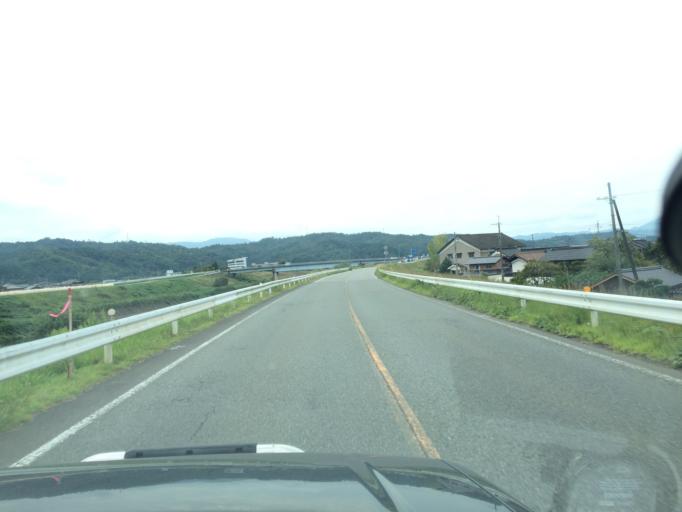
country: JP
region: Hyogo
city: Toyooka
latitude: 35.5108
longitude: 134.8295
